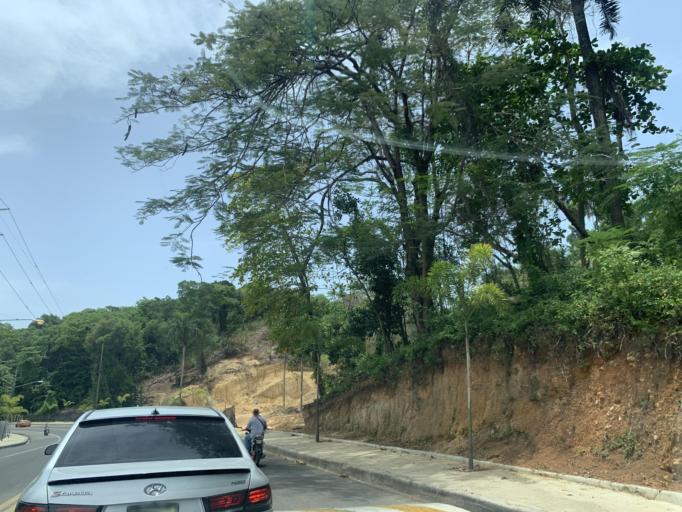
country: DO
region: Puerto Plata
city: Cabarete
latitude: 19.7533
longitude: -70.5178
